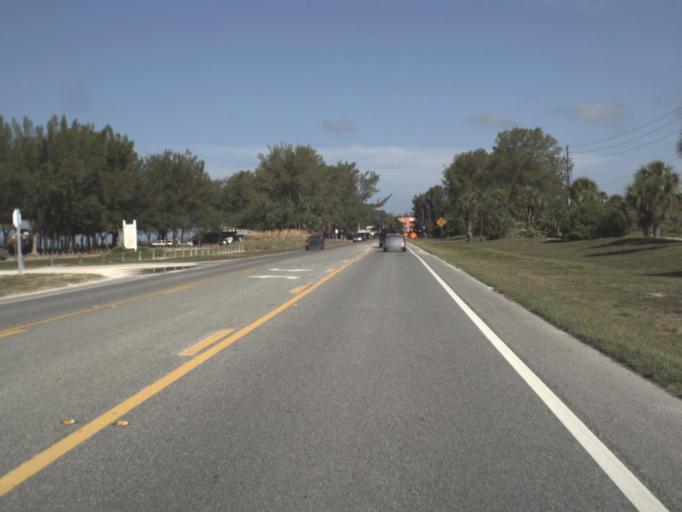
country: US
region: Florida
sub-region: Manatee County
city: Cortez
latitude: 27.4533
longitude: -82.6929
